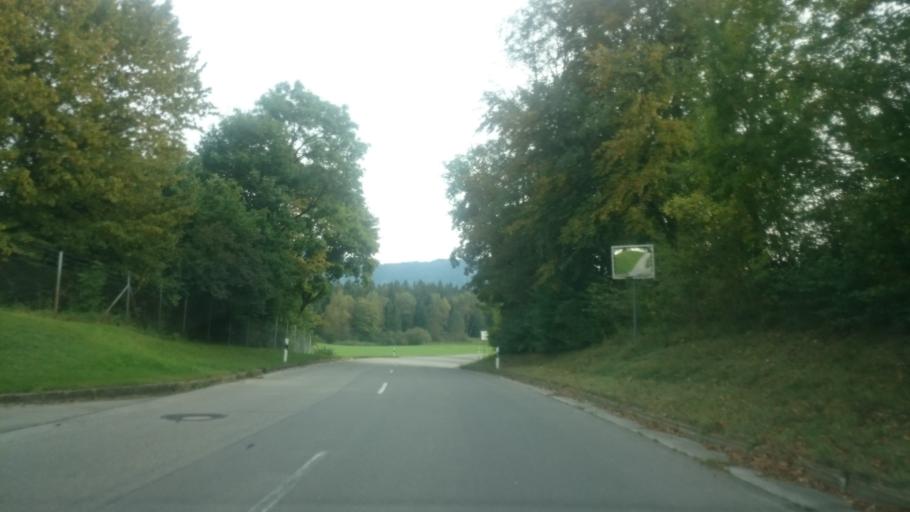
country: AT
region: Tyrol
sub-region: Politischer Bezirk Reutte
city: Vils
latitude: 47.5820
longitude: 10.6521
